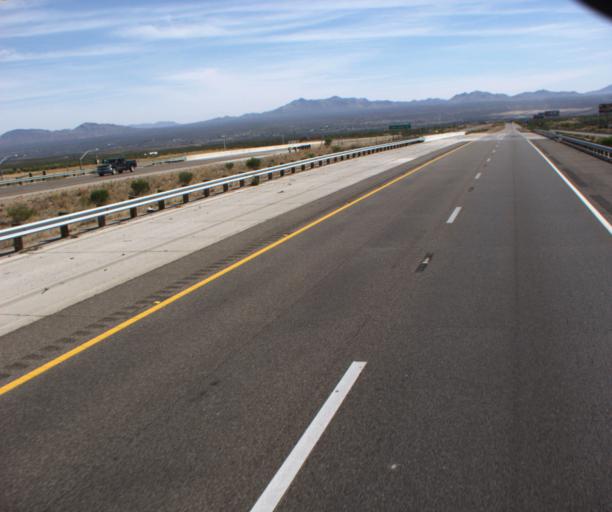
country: US
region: Arizona
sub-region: Cochise County
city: Whetstone
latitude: 31.9641
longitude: -110.3479
